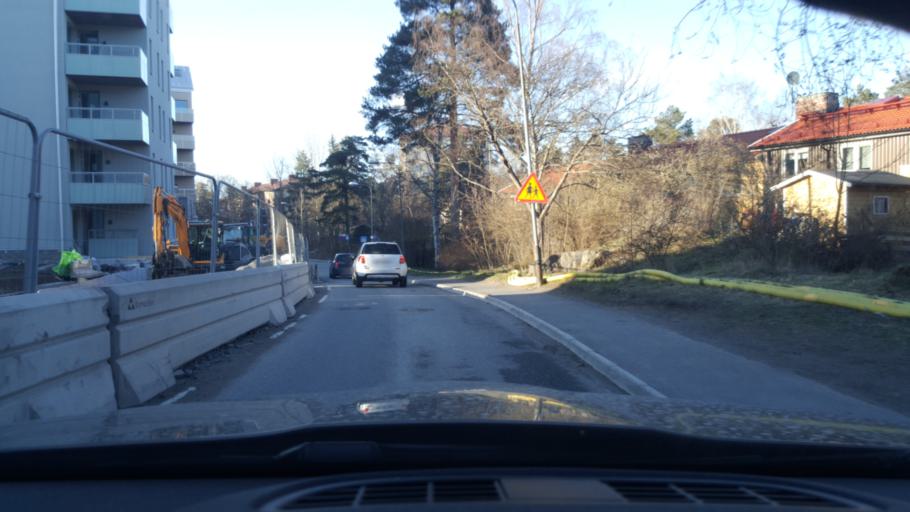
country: SE
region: Stockholm
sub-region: Stockholms Kommun
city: Arsta
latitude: 59.2652
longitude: 18.0567
